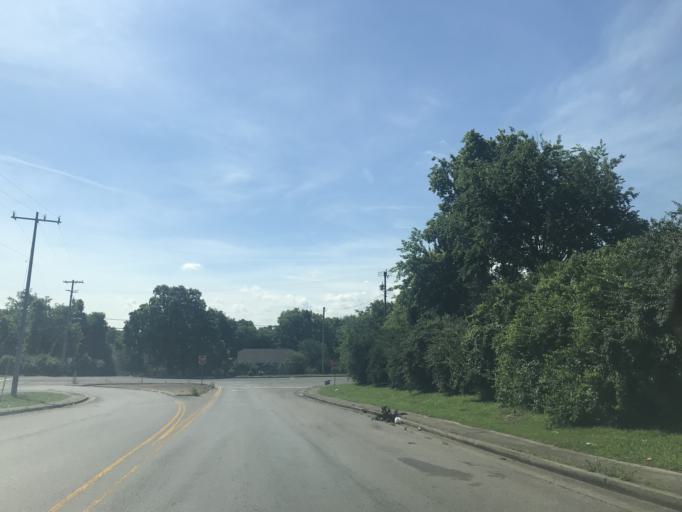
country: US
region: Tennessee
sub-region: Davidson County
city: Nashville
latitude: 36.1929
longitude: -86.8330
